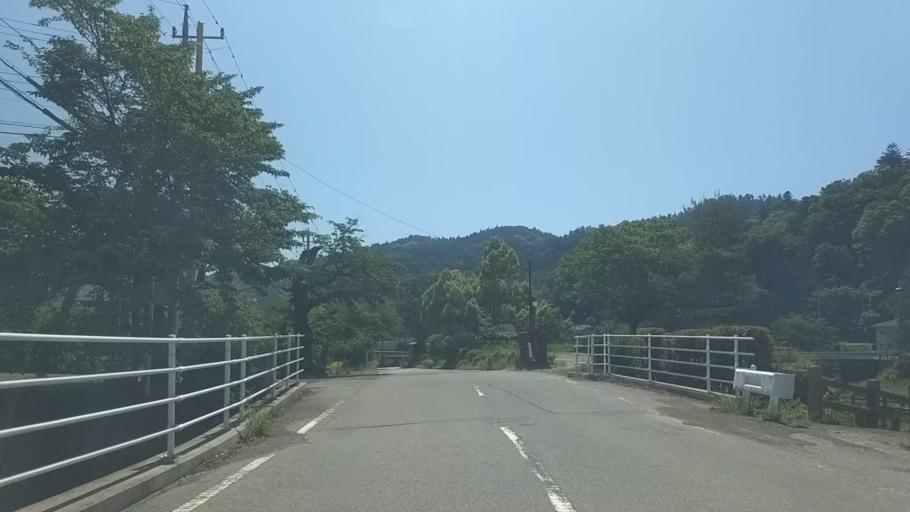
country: JP
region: Yamanashi
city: Ryuo
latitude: 35.5071
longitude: 138.4244
